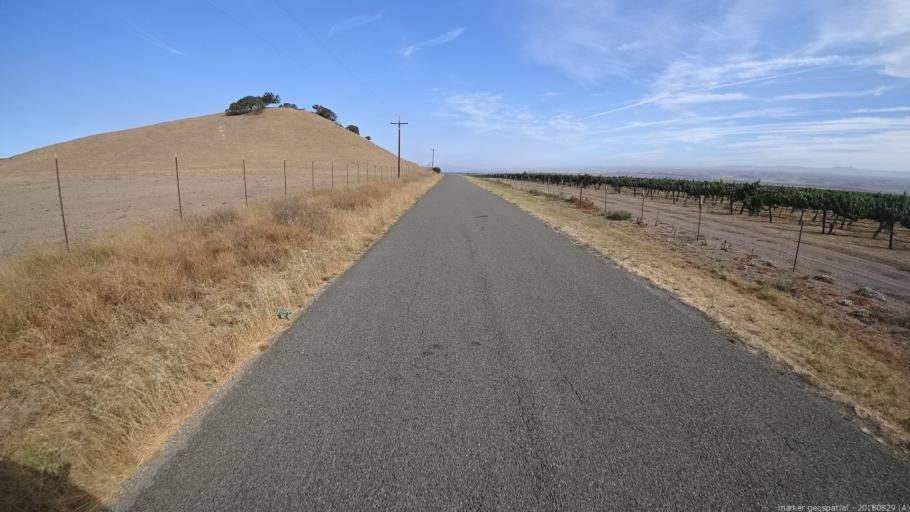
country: US
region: California
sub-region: Monterey County
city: King City
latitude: 36.0783
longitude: -121.0392
